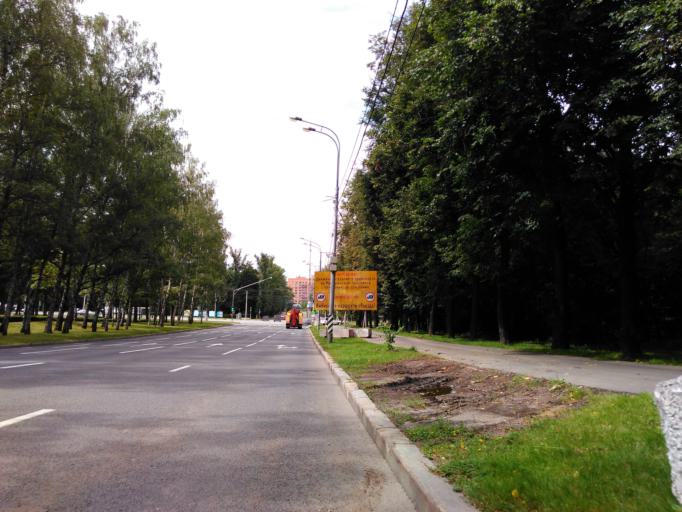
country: RU
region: Moscow
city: Vorob'yovo
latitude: 55.7111
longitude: 37.5293
